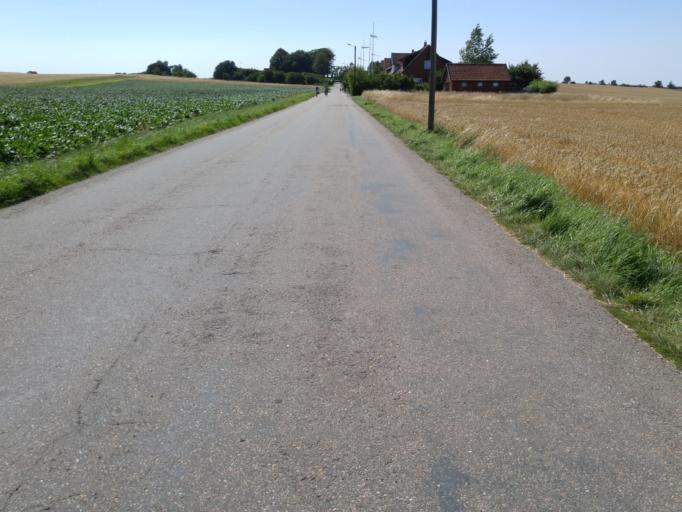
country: SE
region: Skane
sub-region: Helsingborg
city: Rydeback
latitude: 55.9133
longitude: 12.6835
